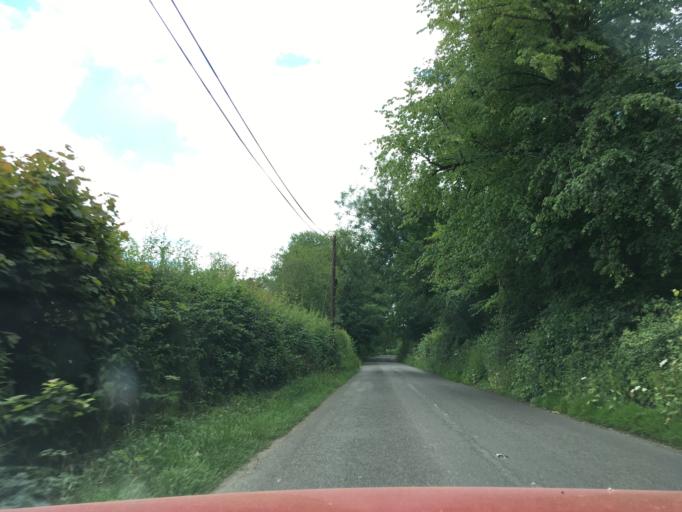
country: GB
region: England
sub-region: West Berkshire
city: Welford
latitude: 51.4562
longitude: -1.4103
